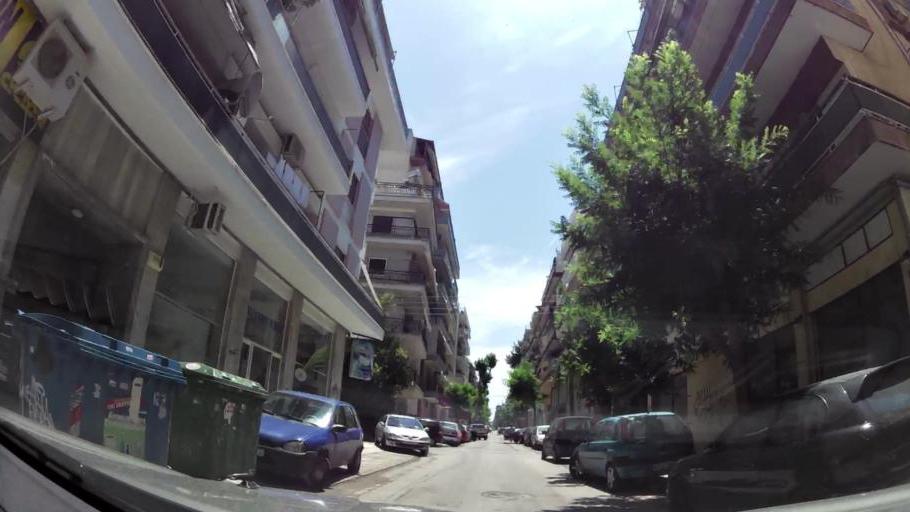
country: GR
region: Central Macedonia
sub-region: Nomos Thessalonikis
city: Triandria
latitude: 40.6110
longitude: 22.9595
